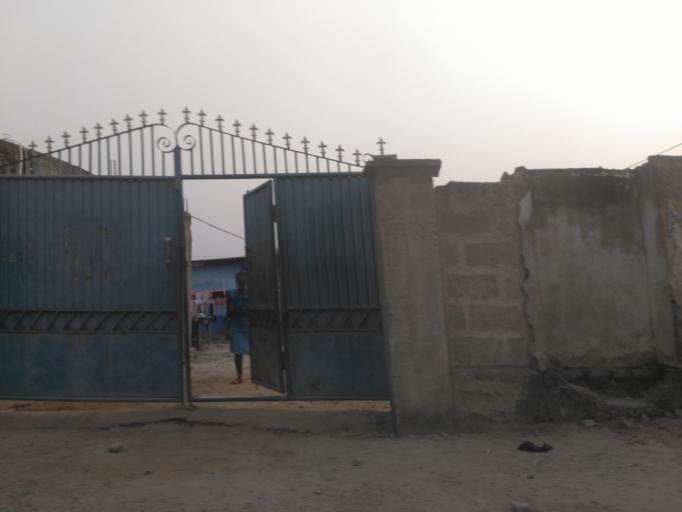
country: GH
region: Ashanti
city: Tafo
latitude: 6.7098
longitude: -1.6117
